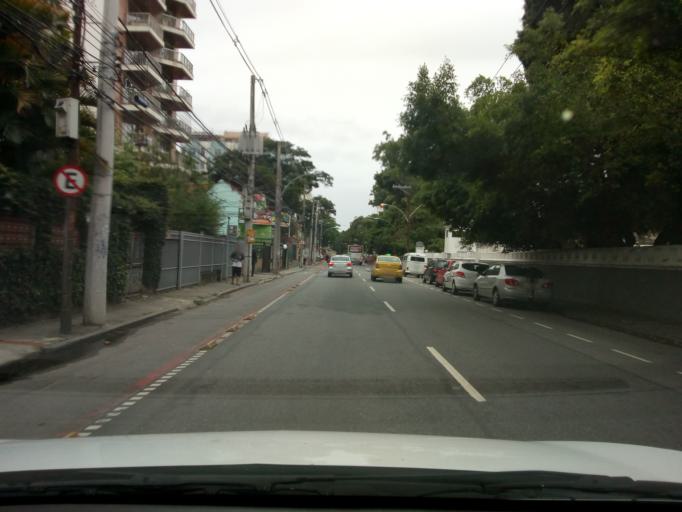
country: BR
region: Rio de Janeiro
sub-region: Rio De Janeiro
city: Rio de Janeiro
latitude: -22.9185
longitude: -43.2301
